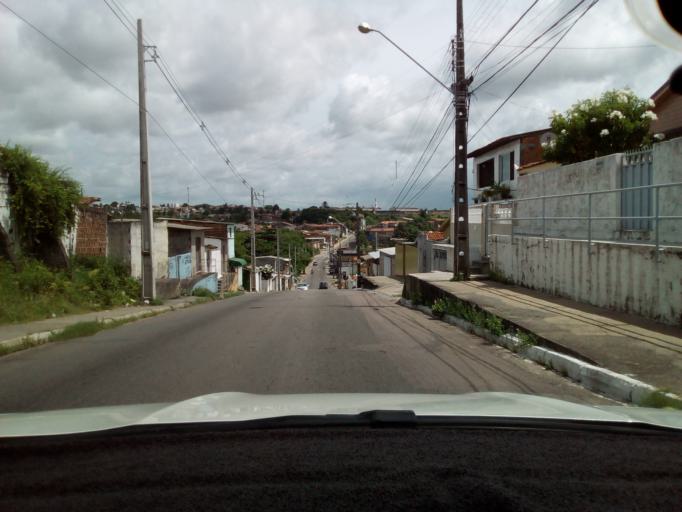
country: BR
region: Paraiba
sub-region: Joao Pessoa
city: Joao Pessoa
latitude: -7.1065
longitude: -34.8706
